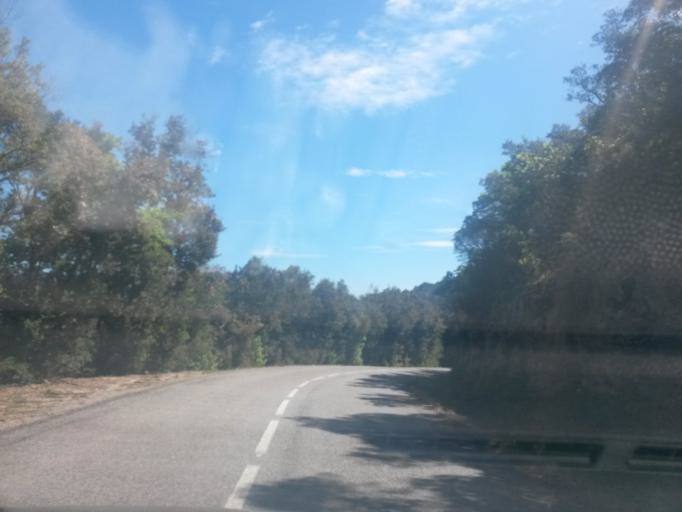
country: ES
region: Catalonia
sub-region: Provincia de Girona
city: Sant Marti Vell
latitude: 41.9820
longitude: 2.9255
